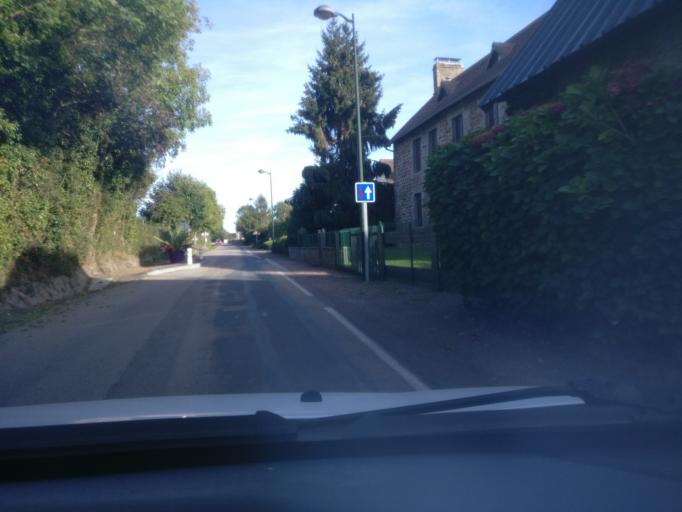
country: FR
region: Lower Normandy
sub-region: Departement de la Manche
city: Marcey-les-Greves
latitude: 48.7003
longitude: -1.4398
